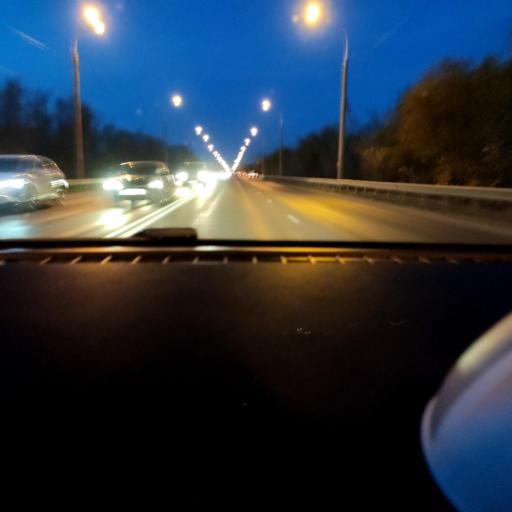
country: RU
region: Samara
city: Samara
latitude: 53.1496
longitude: 50.1856
